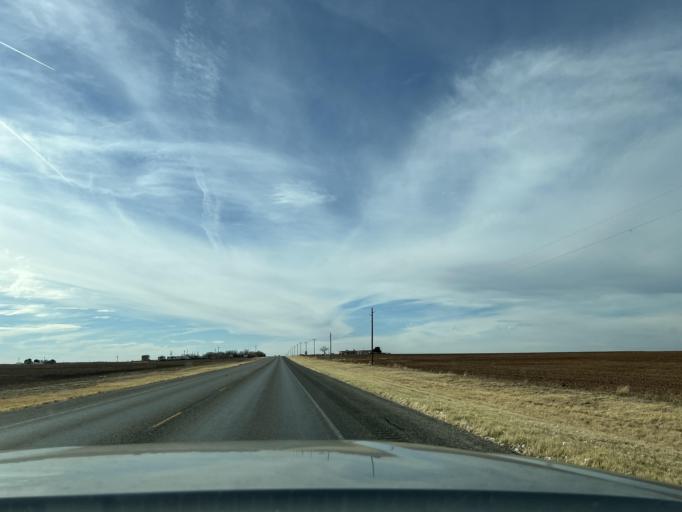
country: US
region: Texas
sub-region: Jones County
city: Anson
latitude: 32.7518
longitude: -99.9118
